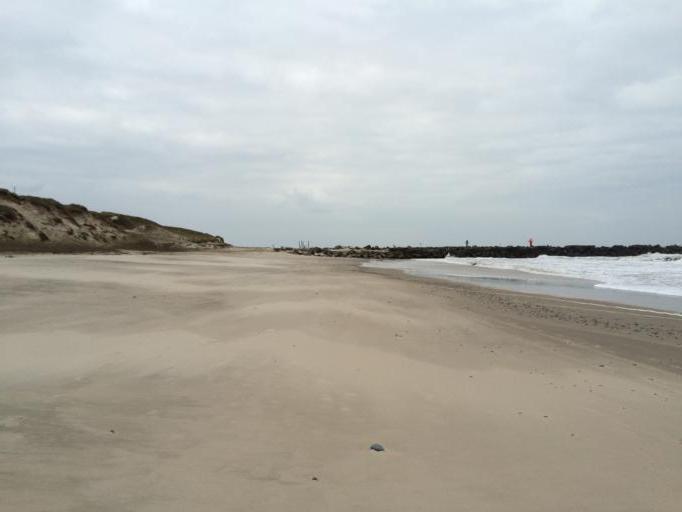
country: DK
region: Central Jutland
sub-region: Holstebro Kommune
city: Ulfborg
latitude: 56.3753
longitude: 8.1168
